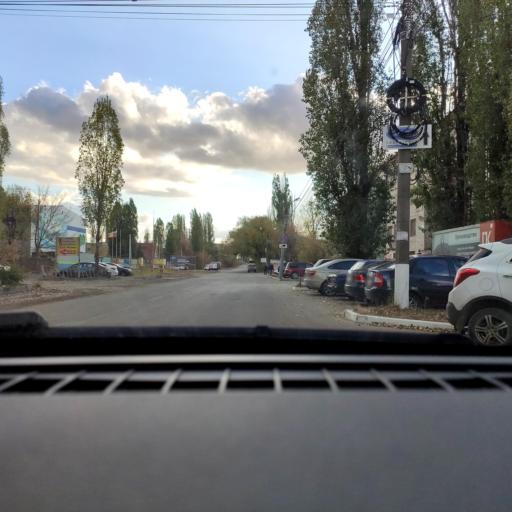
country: RU
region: Voronezj
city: Voronezh
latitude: 51.6508
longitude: 39.2890
